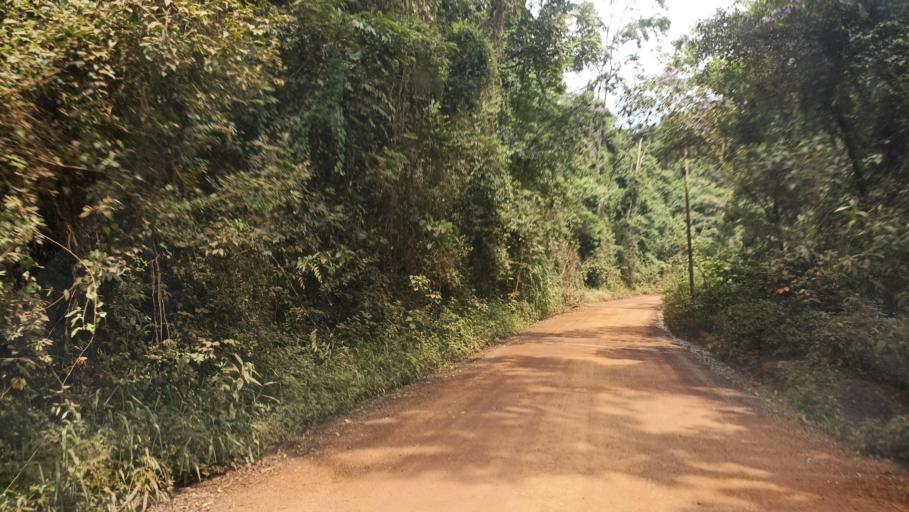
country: BR
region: Minas Gerais
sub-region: Itabirito
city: Itabirito
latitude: -20.3750
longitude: -43.7607
